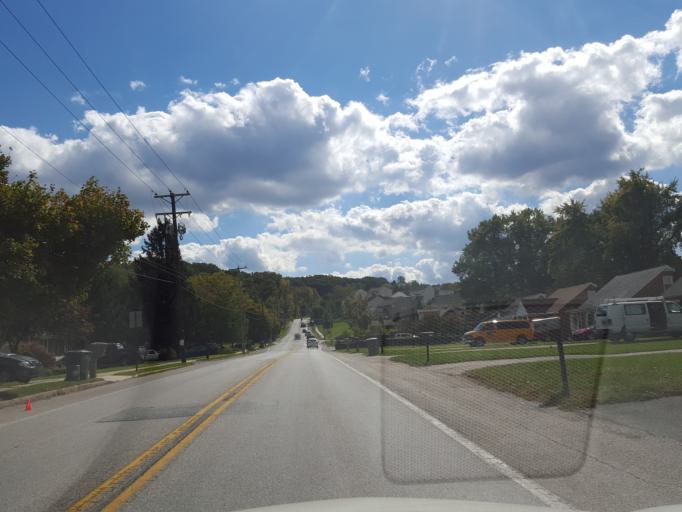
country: US
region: Pennsylvania
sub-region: York County
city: Stonybrook
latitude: 39.9718
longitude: -76.6599
